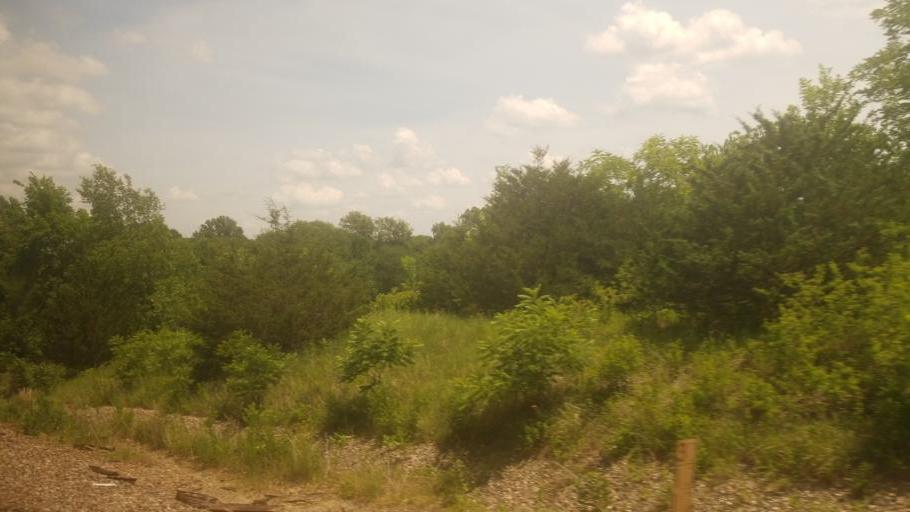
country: US
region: Missouri
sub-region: Macon County
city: La Plata
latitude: 40.0453
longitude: -92.4713
